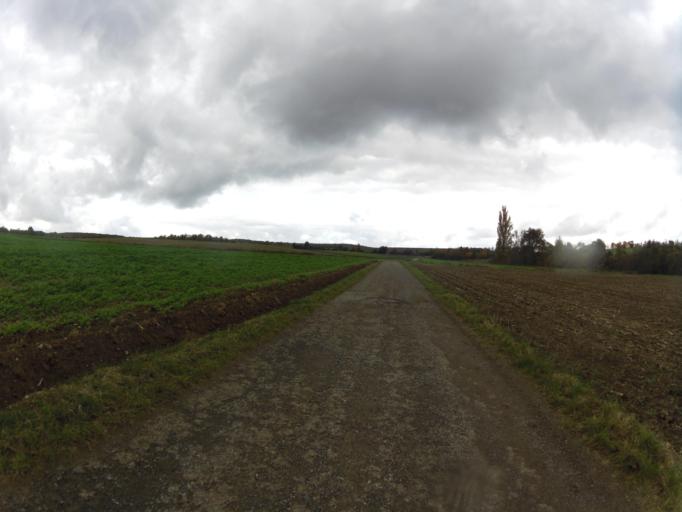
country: DE
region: Bavaria
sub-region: Regierungsbezirk Unterfranken
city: Kurnach
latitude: 49.8705
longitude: 10.0110
